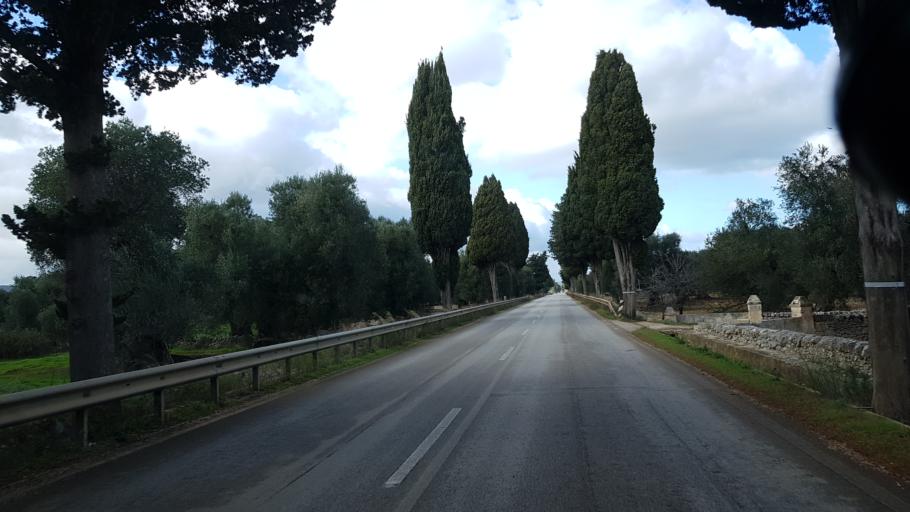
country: IT
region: Apulia
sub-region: Provincia di Brindisi
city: Montalbano
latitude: 40.7700
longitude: 17.5078
